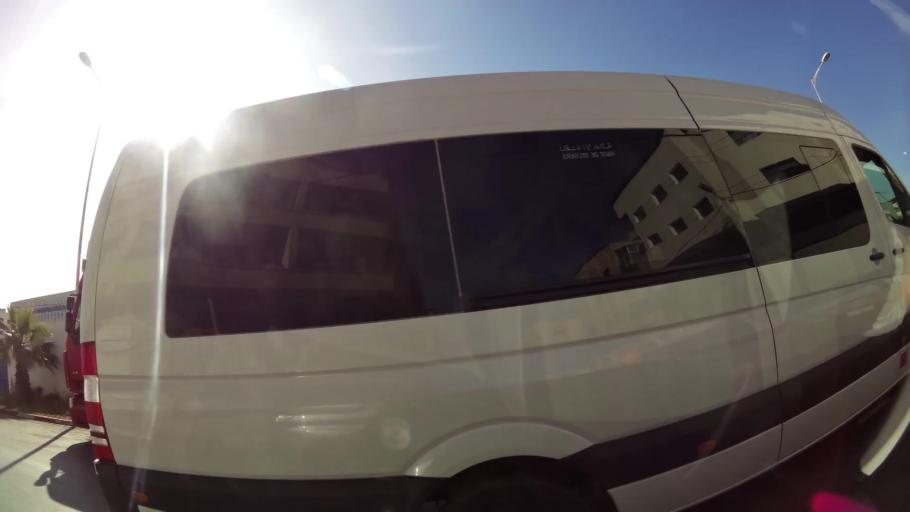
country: MA
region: Rabat-Sale-Zemmour-Zaer
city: Sale
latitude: 34.0562
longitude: -6.8095
